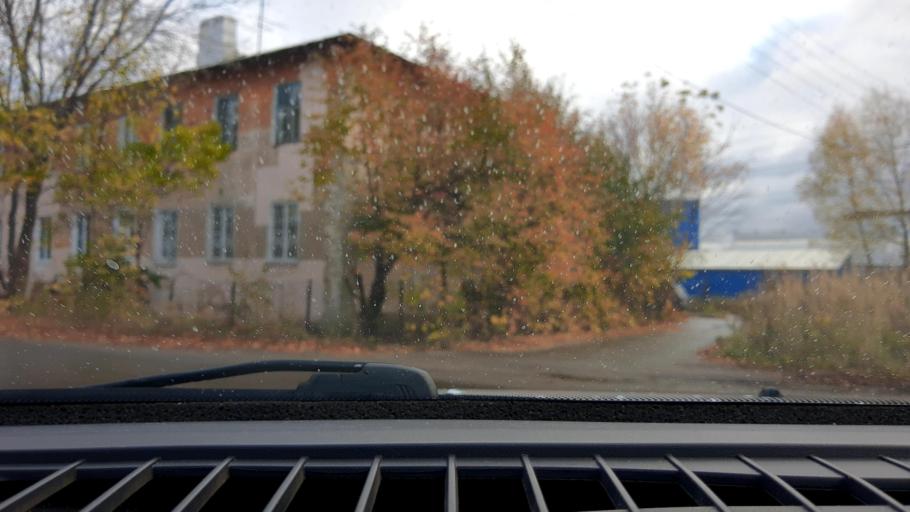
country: RU
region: Nizjnij Novgorod
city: Nizhniy Novgorod
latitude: 56.3013
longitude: 43.8851
